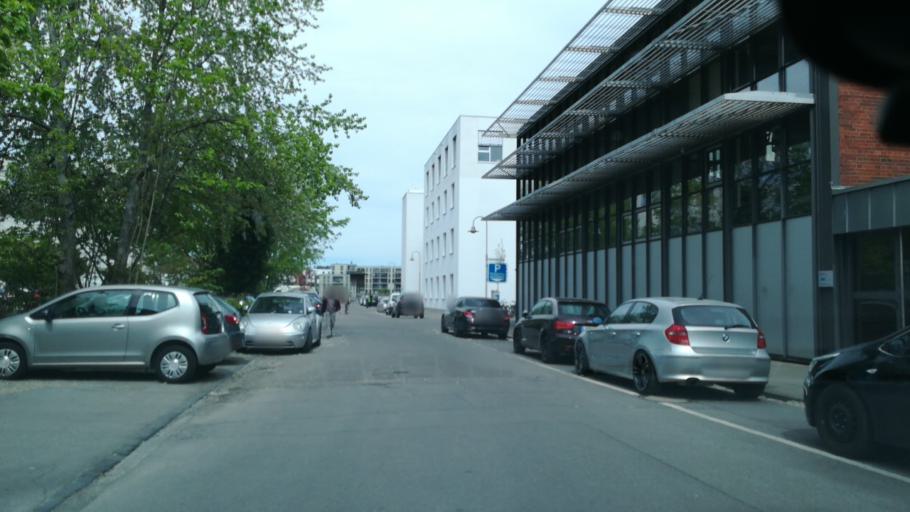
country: DE
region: Baden-Wuerttemberg
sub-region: Freiburg Region
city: Konstanz
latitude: 47.6677
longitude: 9.1692
